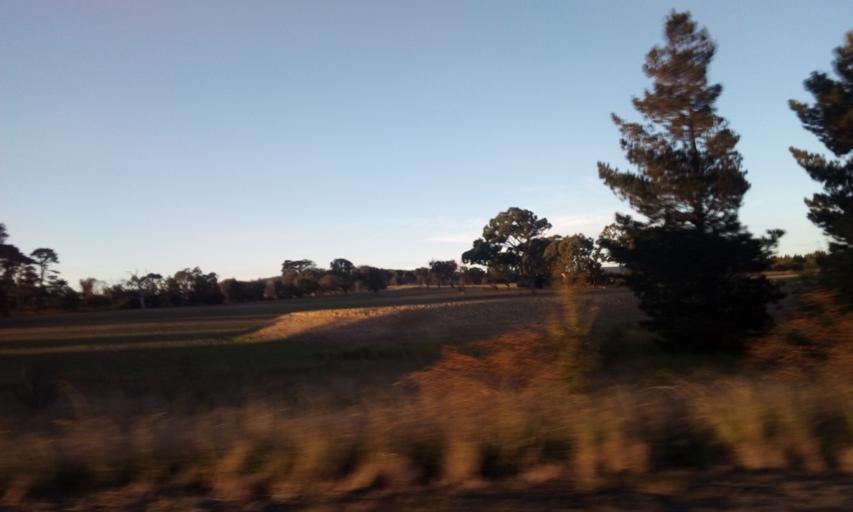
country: AU
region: New South Wales
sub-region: Goulburn Mulwaree
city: Goulburn
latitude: -34.7869
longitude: 149.6308
